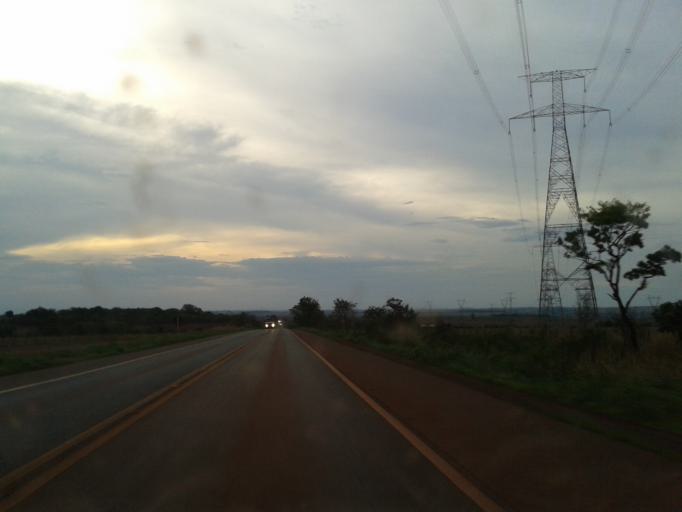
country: BR
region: Goias
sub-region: Santa Helena De Goias
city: Santa Helena de Goias
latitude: -17.9051
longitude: -50.6337
